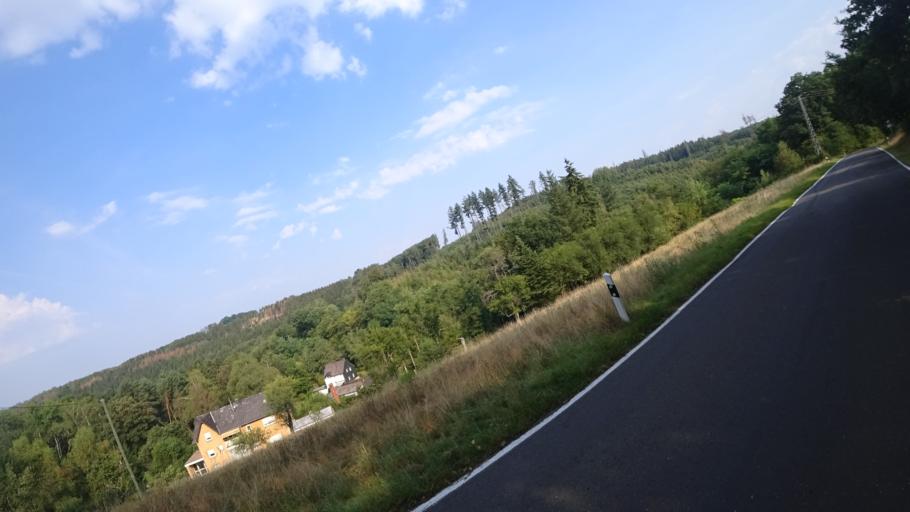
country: DE
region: Rheinland-Pfalz
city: Kammerforst
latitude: 50.4643
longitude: 7.6796
